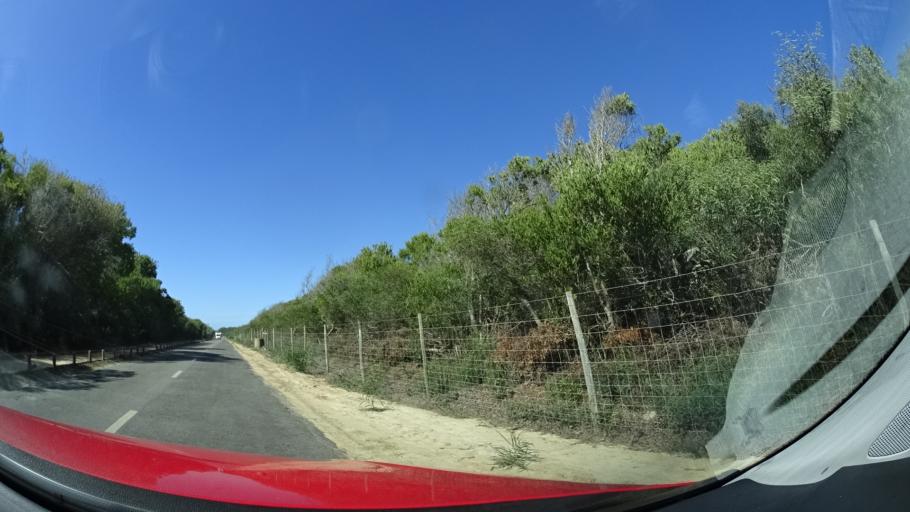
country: PT
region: Beja
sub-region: Odemira
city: Sao Teotonio
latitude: 37.5420
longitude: -8.7874
